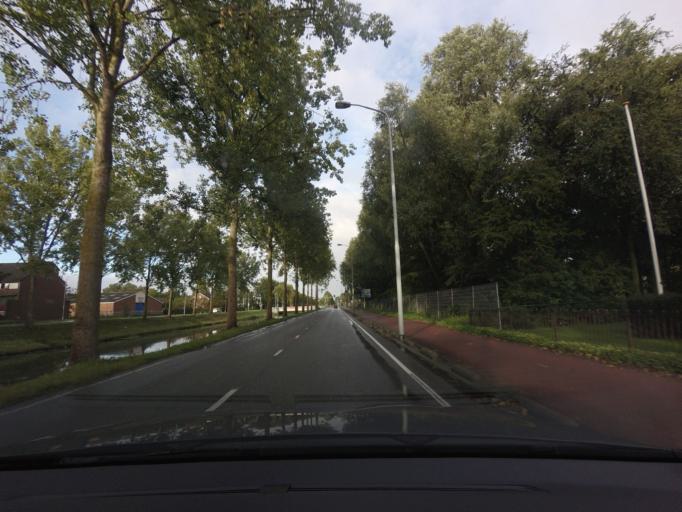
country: NL
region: South Holland
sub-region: Gemeente Kaag en Braassem
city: Oude Wetering
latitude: 52.2595
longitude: 4.6271
